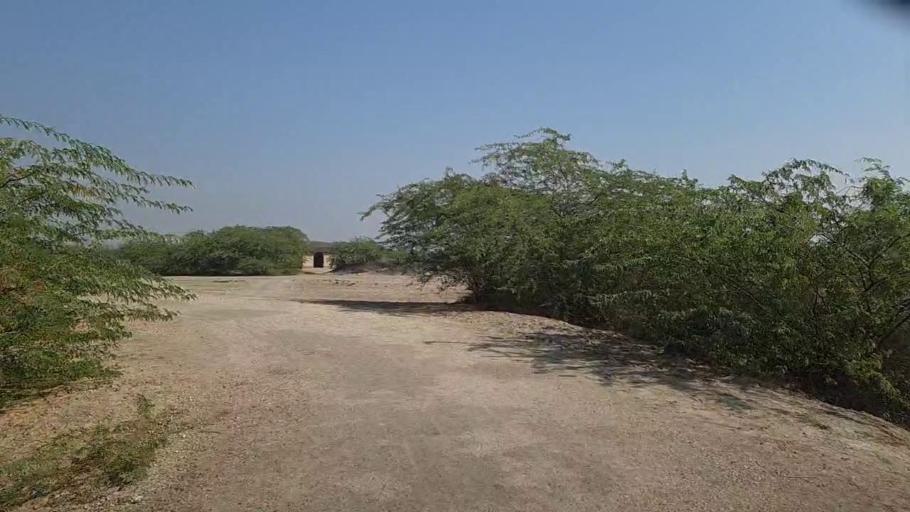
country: PK
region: Sindh
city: Bozdar
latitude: 27.2522
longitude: 68.5976
